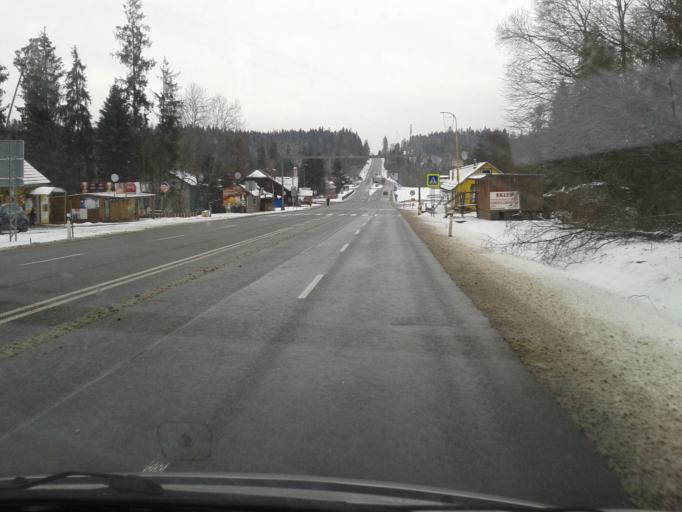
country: PL
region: Lesser Poland Voivodeship
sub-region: Powiat nowotarski
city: Chyzne
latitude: 49.4050
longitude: 19.6557
